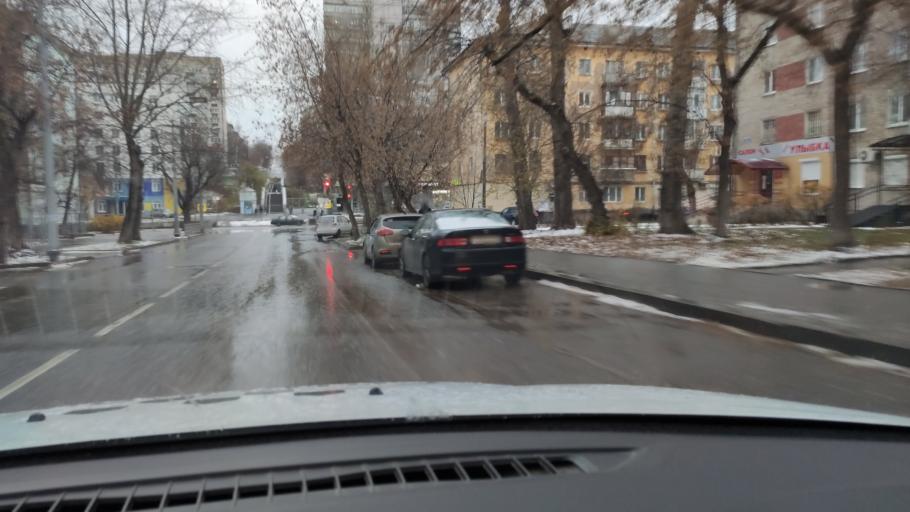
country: RU
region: Perm
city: Perm
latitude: 58.0063
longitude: 56.2057
